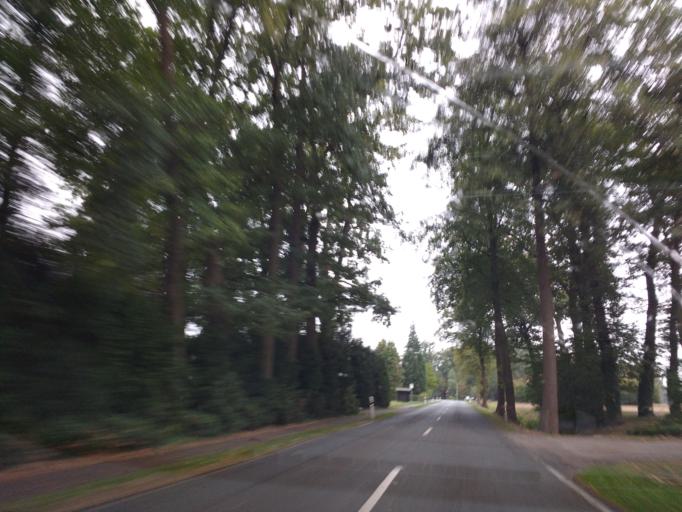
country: DE
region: North Rhine-Westphalia
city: Rietberg
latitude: 51.7382
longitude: 8.4433
